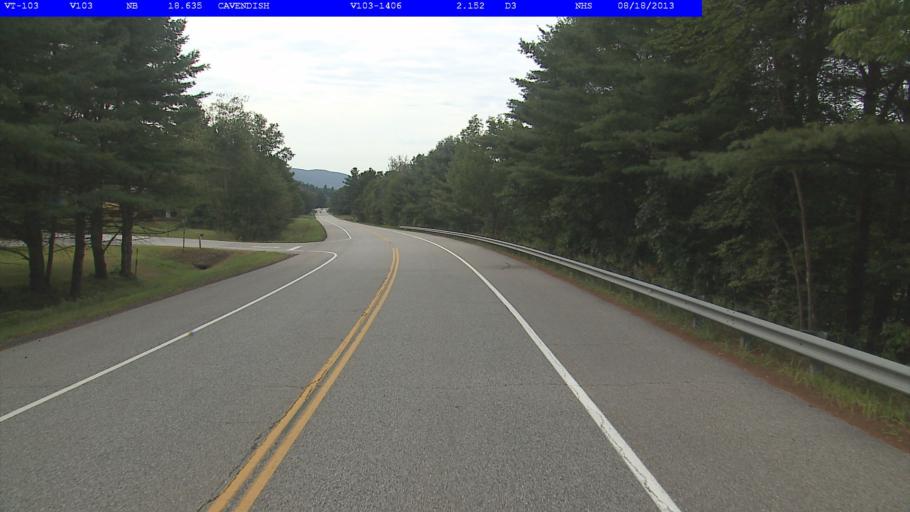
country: US
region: Vermont
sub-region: Windsor County
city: Chester
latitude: 43.3771
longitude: -72.6360
